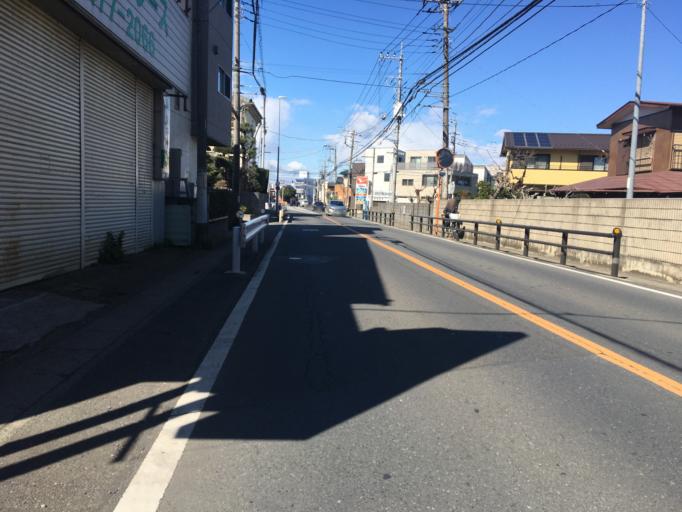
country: JP
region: Saitama
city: Shiki
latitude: 35.8064
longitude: 139.5571
